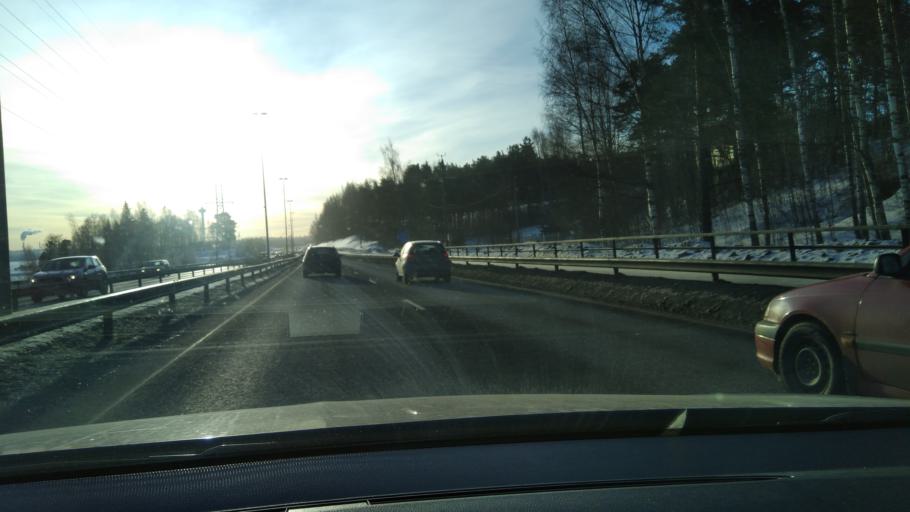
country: FI
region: Pirkanmaa
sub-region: Tampere
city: Pirkkala
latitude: 61.5087
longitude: 23.6963
